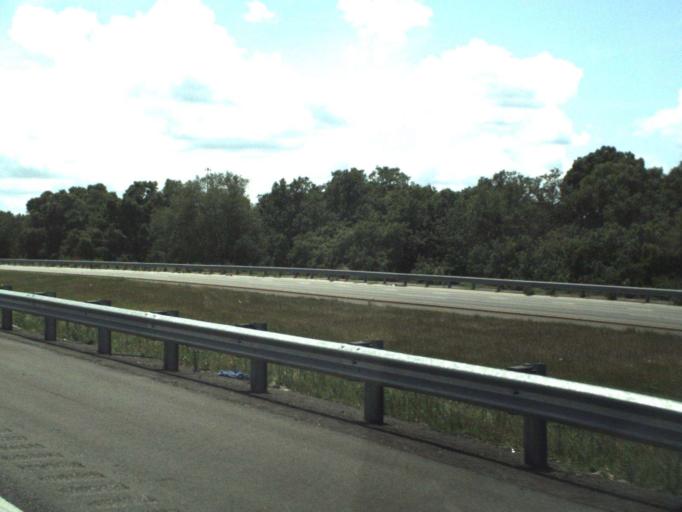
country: US
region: Florida
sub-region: Seminole County
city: Heathrow
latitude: 28.7982
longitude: -81.3448
